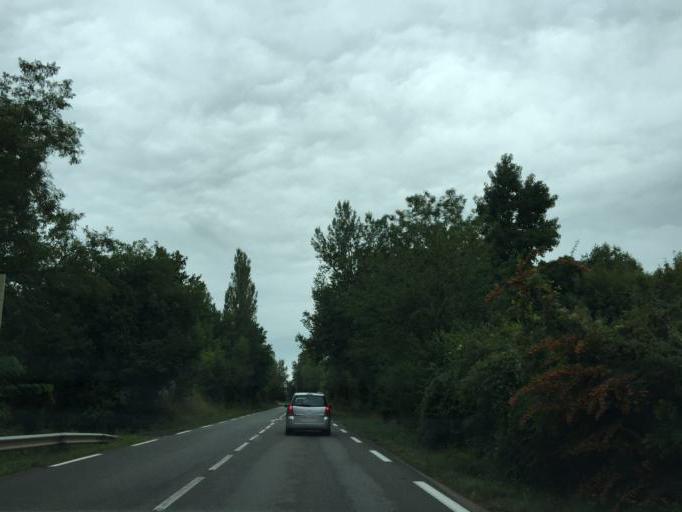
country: FR
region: Midi-Pyrenees
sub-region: Departement de l'Aveyron
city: Espalion
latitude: 44.5140
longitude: 2.7379
